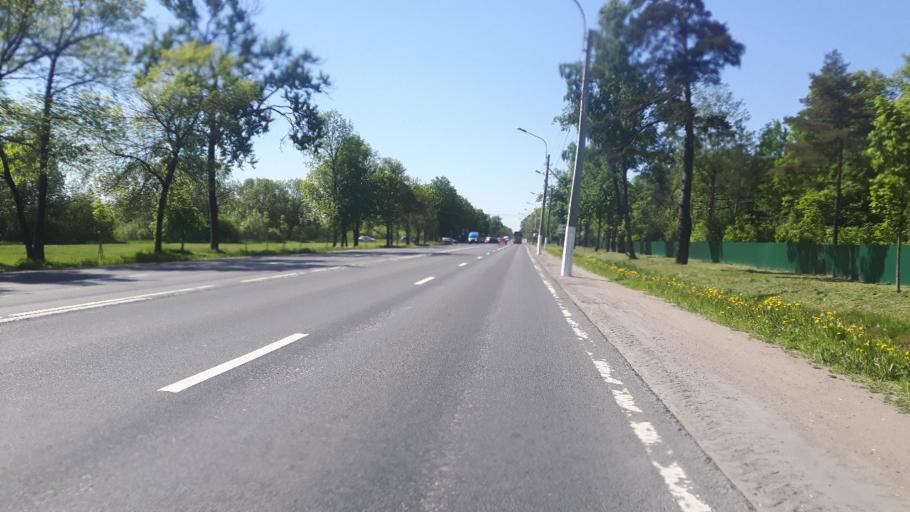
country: RU
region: Leningrad
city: Ol'gino
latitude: 59.8720
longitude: 29.9652
